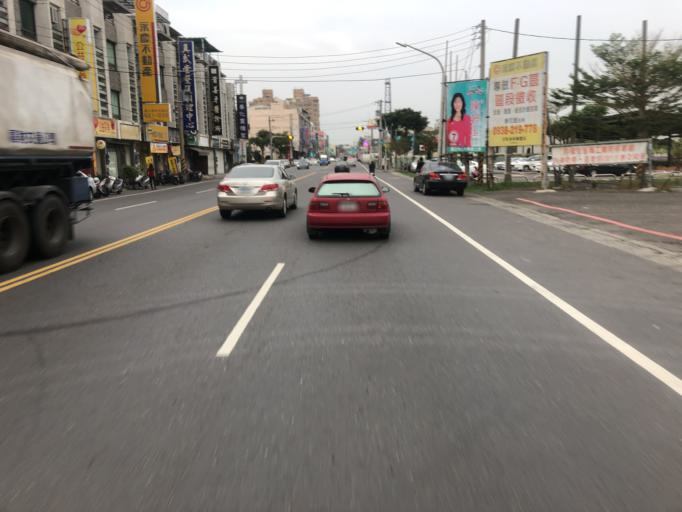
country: TW
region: Taiwan
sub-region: Tainan
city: Tainan
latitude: 23.1275
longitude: 120.2893
